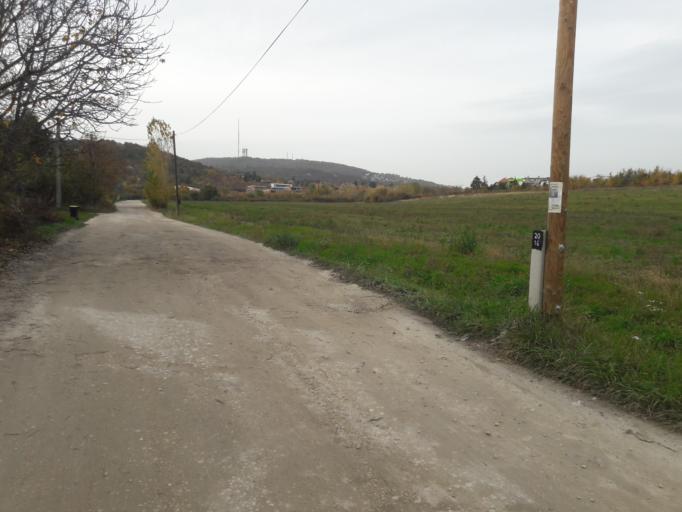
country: HU
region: Pest
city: Budaors
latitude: 47.4683
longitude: 18.9827
